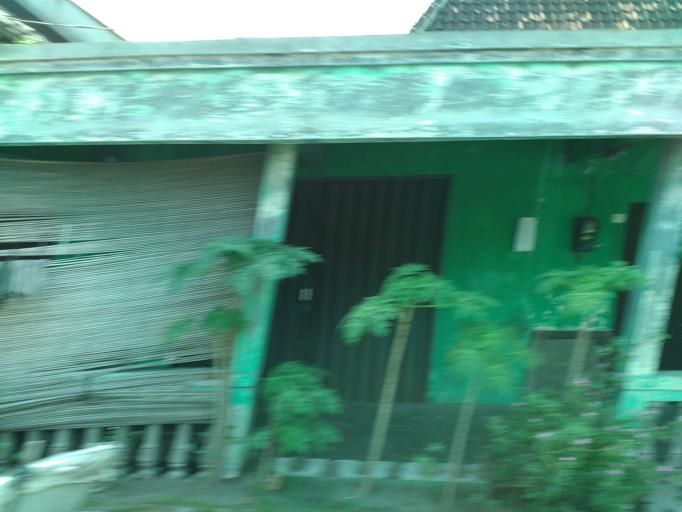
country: ID
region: Central Java
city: Candi Prambanan
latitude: -7.7492
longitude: 110.5220
